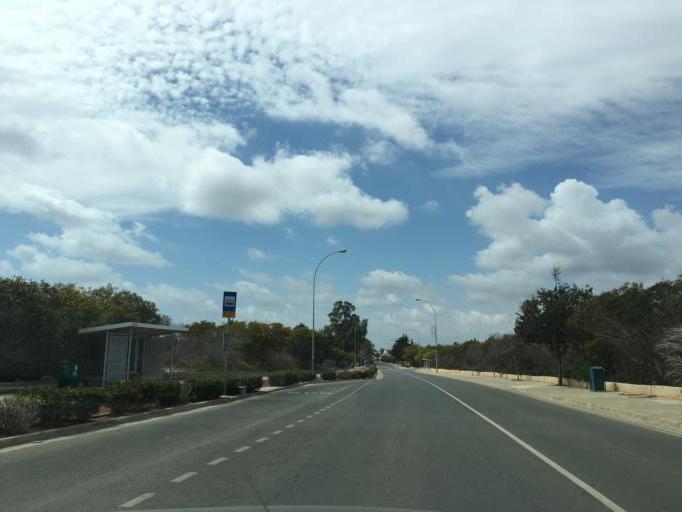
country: CY
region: Ammochostos
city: Ayia Napa
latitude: 34.9889
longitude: 33.9612
